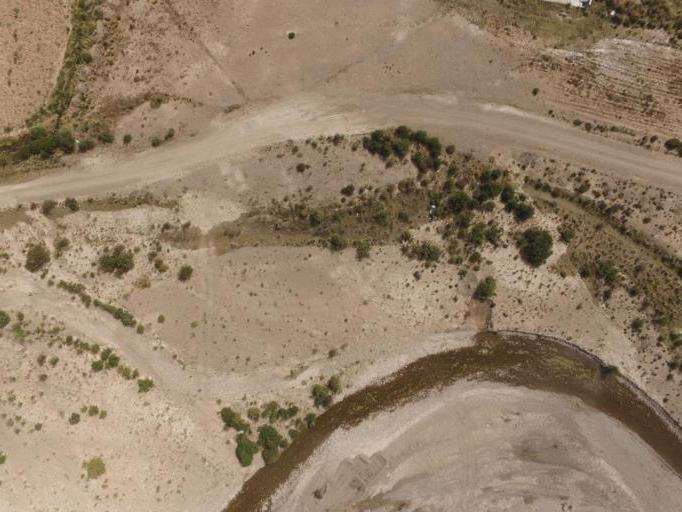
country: BO
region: Oruro
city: Challapata
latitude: -18.6920
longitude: -66.7597
